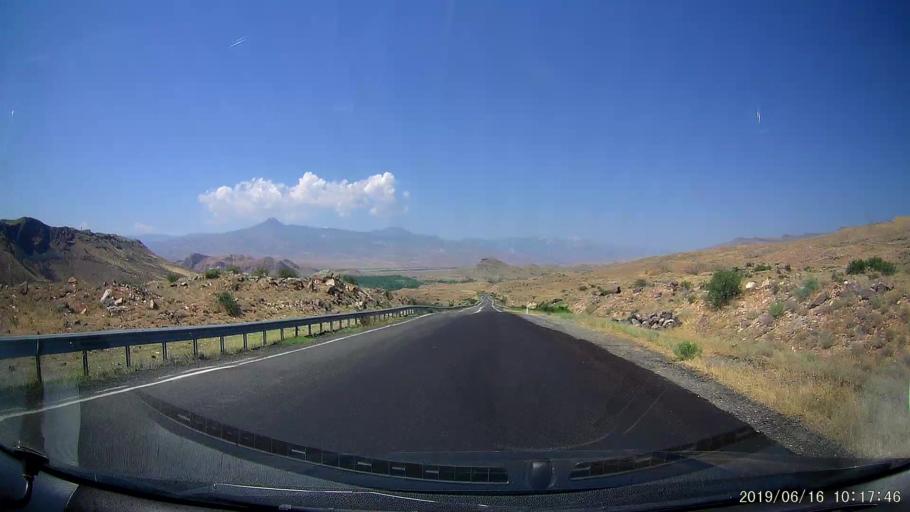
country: TR
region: Igdir
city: Tuzluca
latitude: 40.1643
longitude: 43.6770
